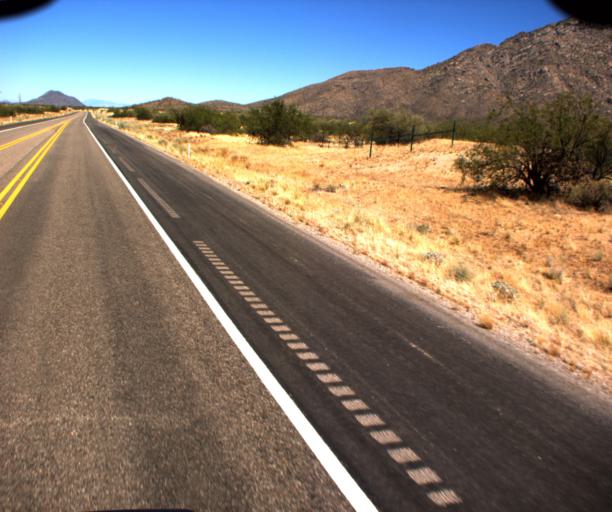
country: US
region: Arizona
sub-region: Pima County
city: Three Points
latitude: 32.0272
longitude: -111.5758
